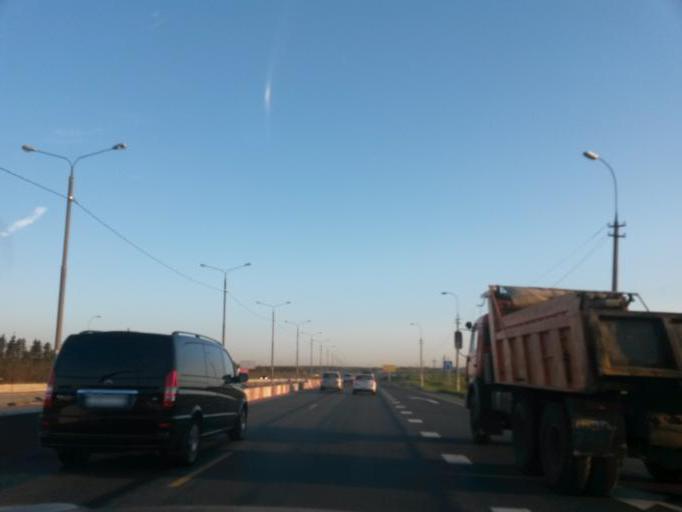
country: RU
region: Moskovskaya
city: Klimovsk
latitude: 55.3575
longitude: 37.5968
